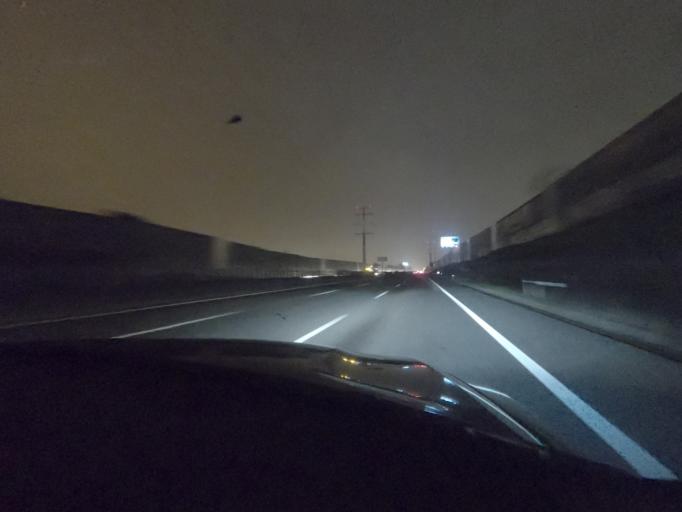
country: PT
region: Lisbon
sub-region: Loures
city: Sao Joao da Talha
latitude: 38.8336
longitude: -9.0966
